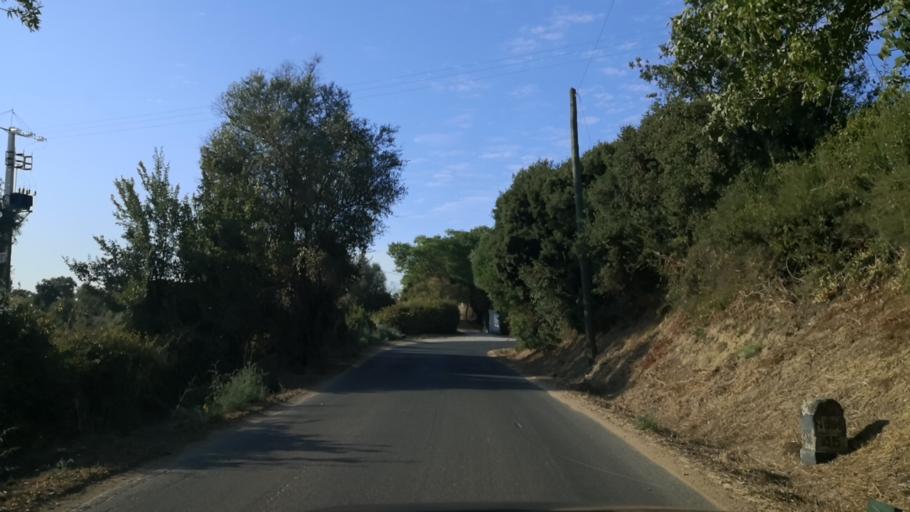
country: PT
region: Santarem
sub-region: Santarem
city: Santarem
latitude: 39.2715
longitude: -8.6632
